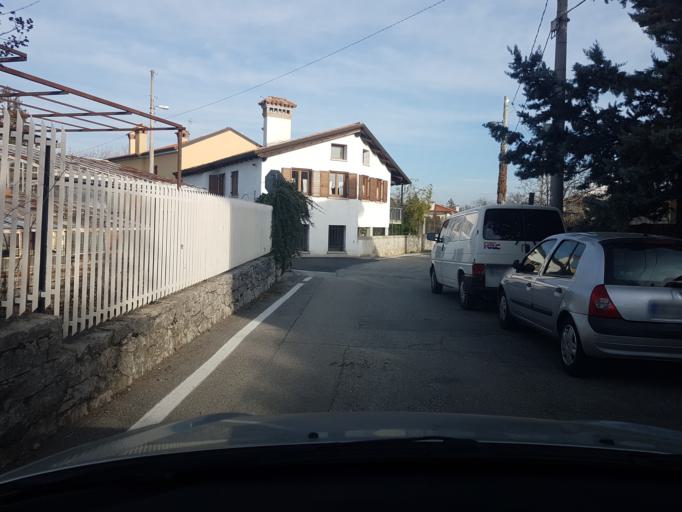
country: IT
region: Friuli Venezia Giulia
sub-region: Provincia di Trieste
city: Prosecco-Contovello
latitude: 45.7094
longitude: 13.7358
